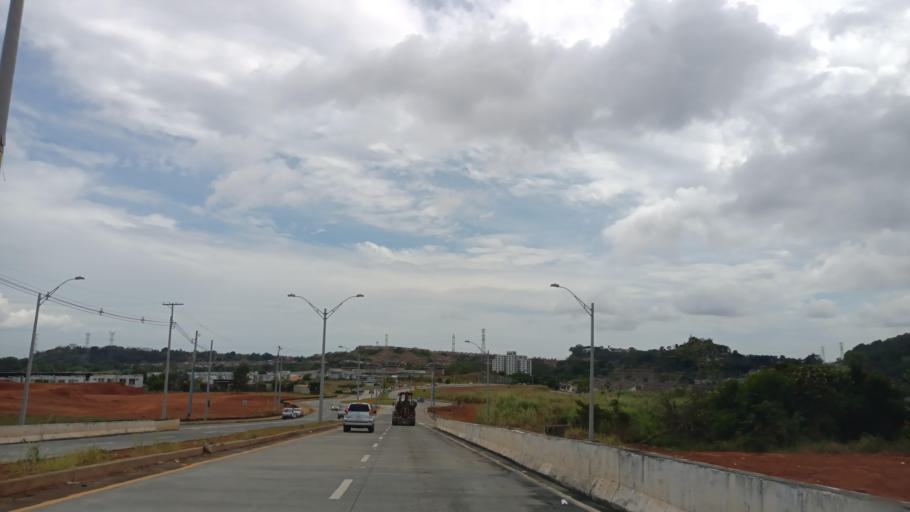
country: PA
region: Panama
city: San Miguelito
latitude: 9.0897
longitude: -79.4620
